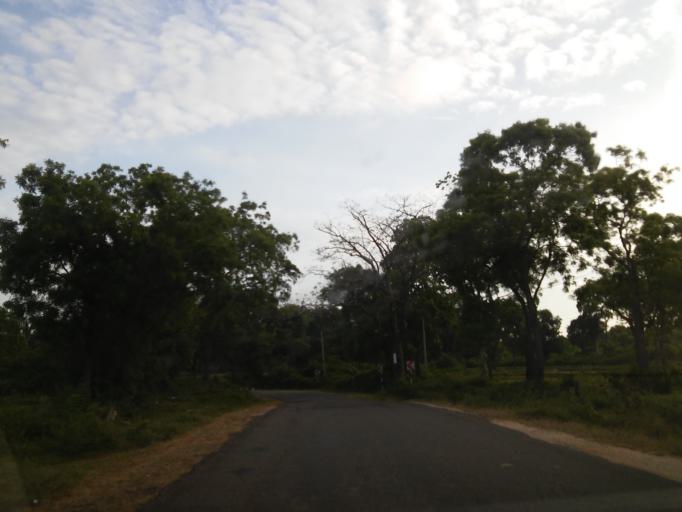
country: LK
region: Central
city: Sigiriya
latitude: 8.1167
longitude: 80.6327
